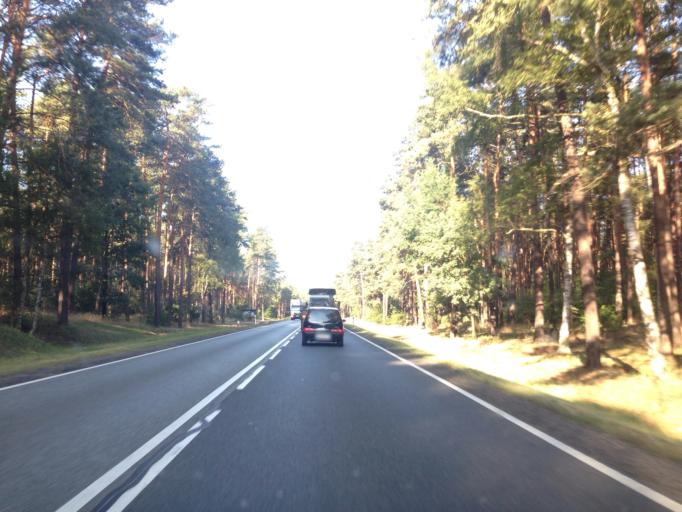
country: PL
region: Kujawsko-Pomorskie
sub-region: Bydgoszcz
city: Bydgoszcz
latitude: 53.0539
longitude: 18.0574
